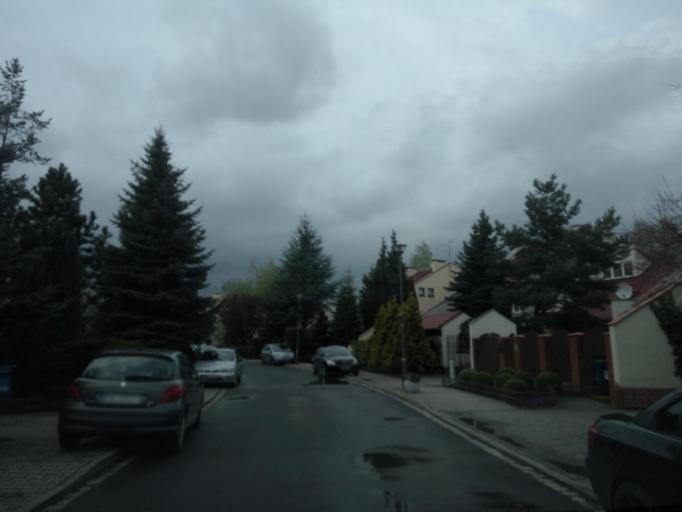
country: PL
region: Lower Silesian Voivodeship
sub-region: Powiat wroclawski
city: Zerniki Wroclawskie
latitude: 51.0598
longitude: 17.0365
